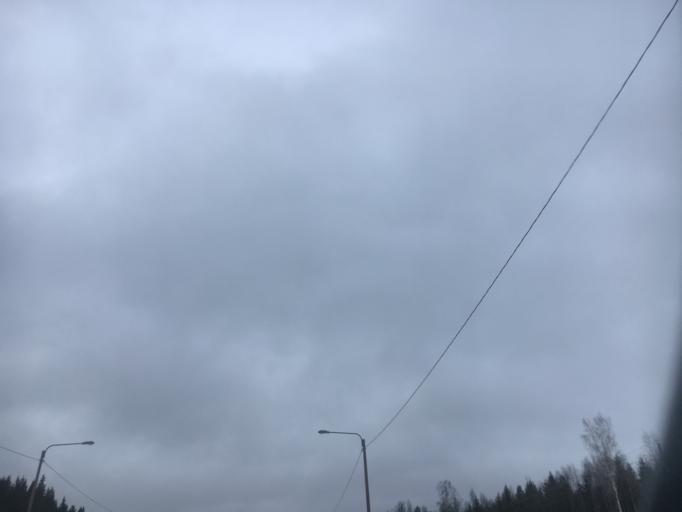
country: FI
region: Central Finland
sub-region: Joutsa
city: Joutsa
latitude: 61.7968
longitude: 26.0942
